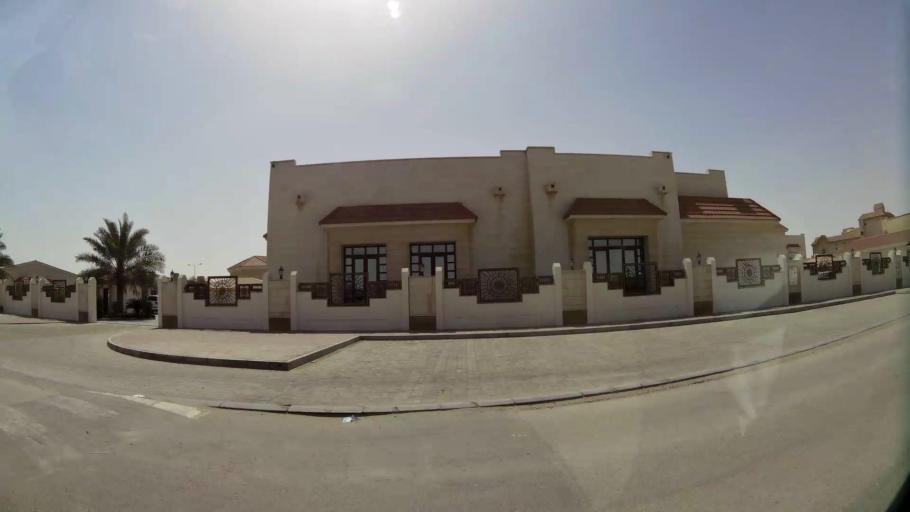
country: QA
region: Baladiyat Umm Salal
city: Umm Salal Muhammad
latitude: 25.3642
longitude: 51.4441
